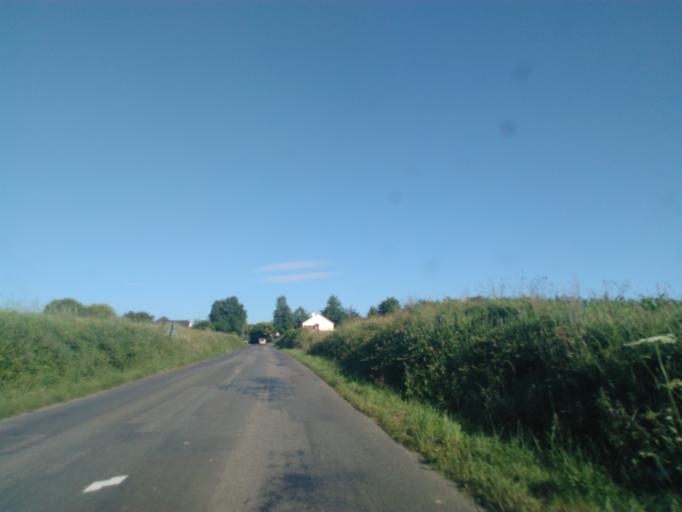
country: FR
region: Brittany
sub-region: Departement d'Ille-et-Vilaine
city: La Meziere
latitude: 48.2232
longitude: -1.7635
